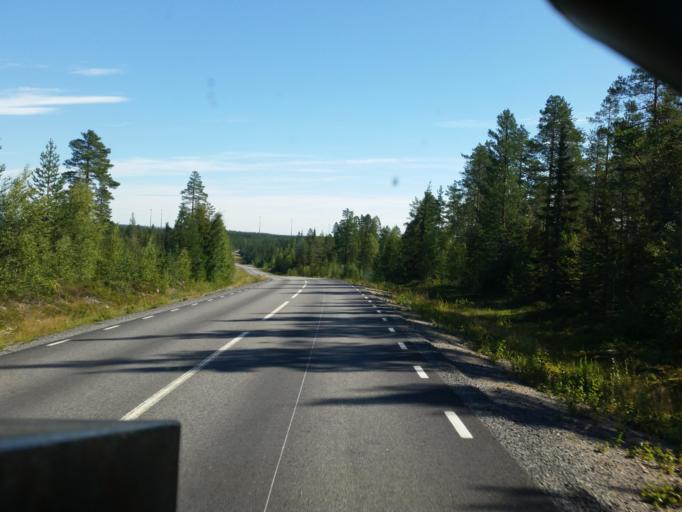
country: SE
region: Vaesterbotten
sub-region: Skelleftea Kommun
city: Storvik
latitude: 65.3315
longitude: 20.8413
